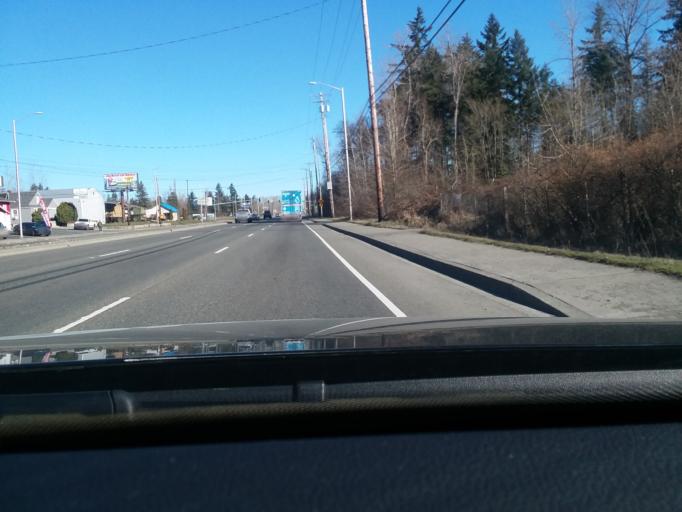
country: US
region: Washington
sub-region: Pierce County
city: Summit
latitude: 47.1306
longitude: -122.3573
